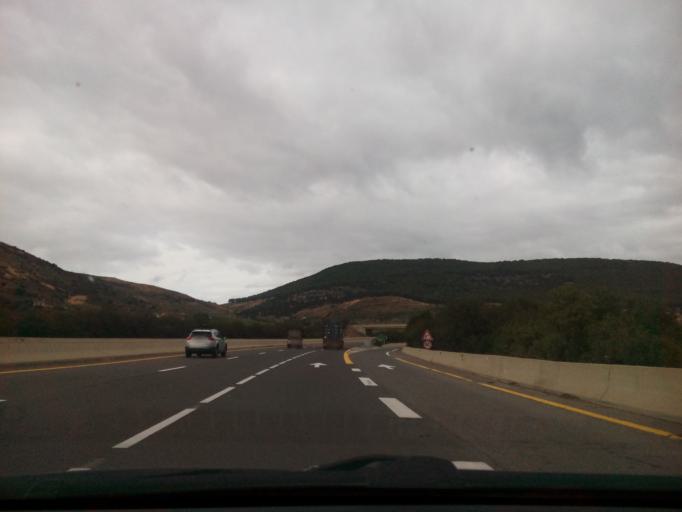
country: DZ
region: Sidi Bel Abbes
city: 'Ain el Berd
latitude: 35.3782
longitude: -0.5008
